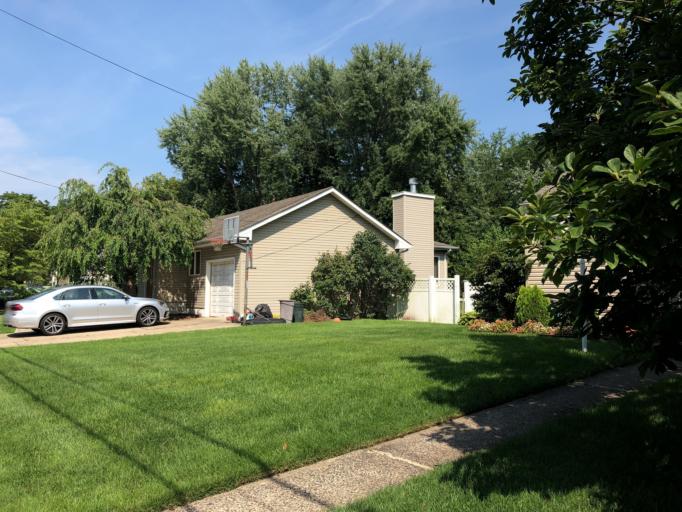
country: US
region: New Jersey
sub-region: Bergen County
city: Fair Lawn
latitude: 40.9447
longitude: -74.1093
